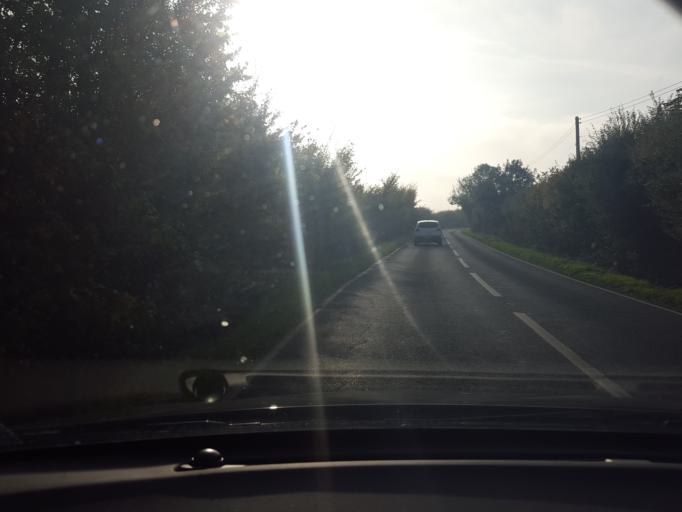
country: GB
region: England
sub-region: Essex
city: Little Clacton
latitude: 51.8878
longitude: 1.1820
